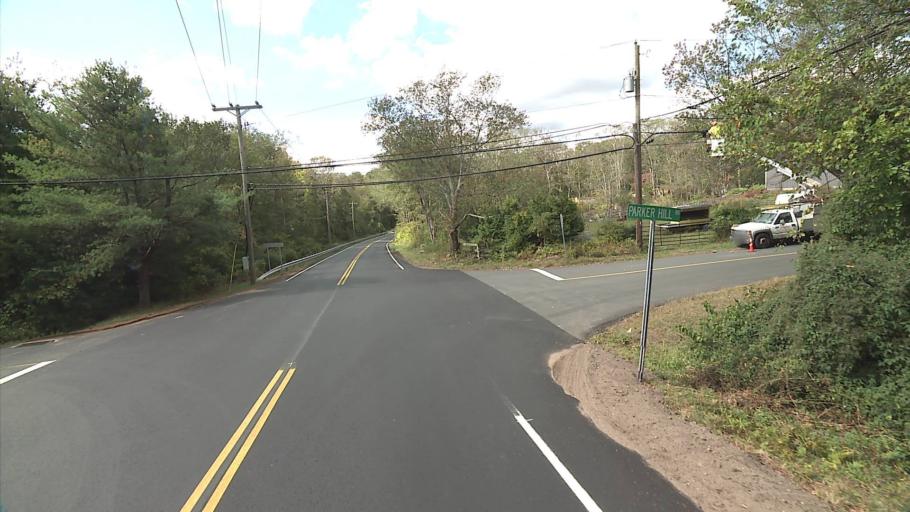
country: US
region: Connecticut
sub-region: Middlesex County
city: Chester Center
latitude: 41.3881
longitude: -72.5302
